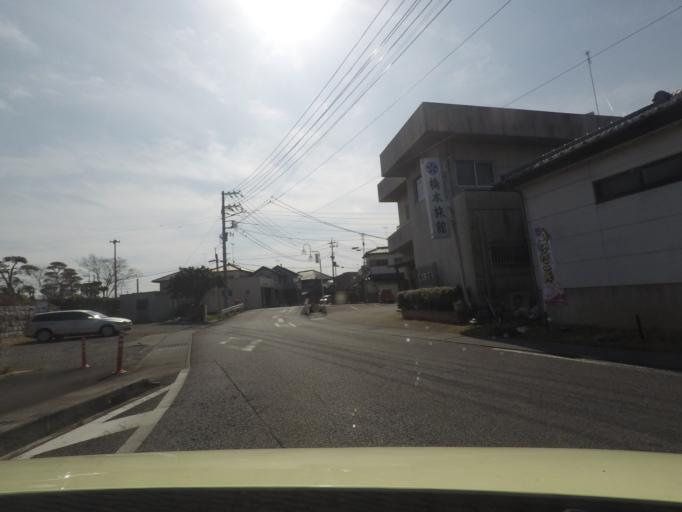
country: JP
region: Ibaraki
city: Ishioka
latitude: 36.1710
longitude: 140.3532
